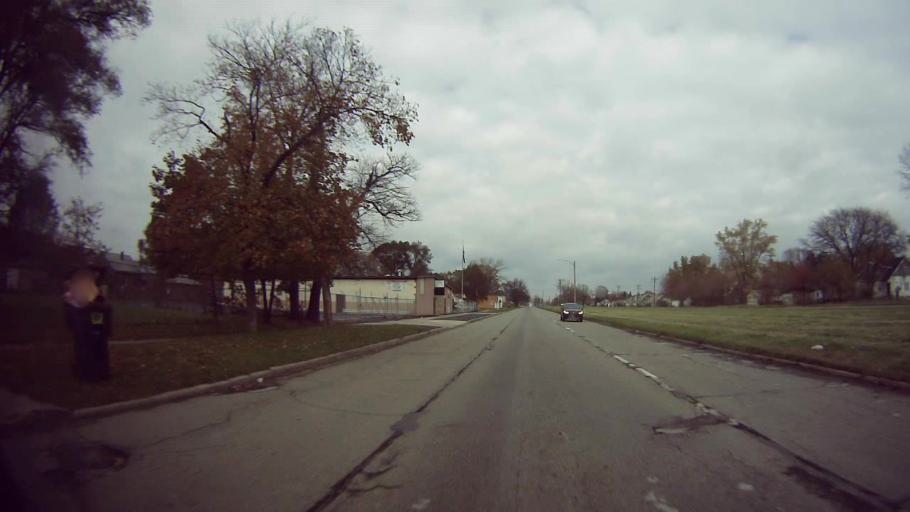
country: US
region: Michigan
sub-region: Wayne County
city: Hamtramck
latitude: 42.4303
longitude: -83.0437
